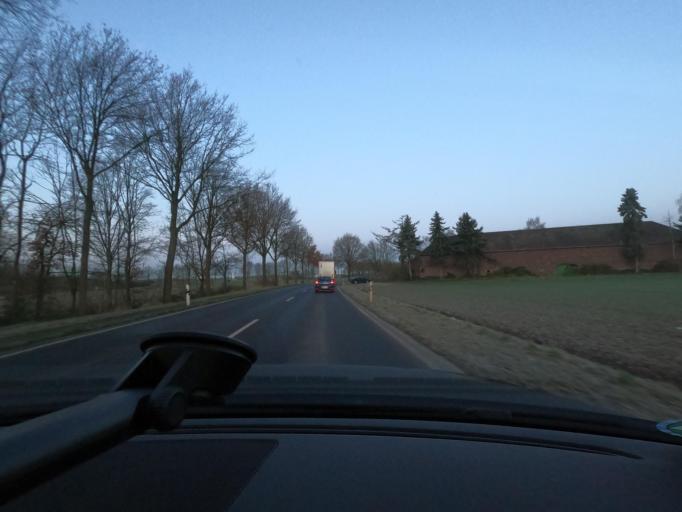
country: DE
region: North Rhine-Westphalia
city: Kempen
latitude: 51.3287
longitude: 6.4266
